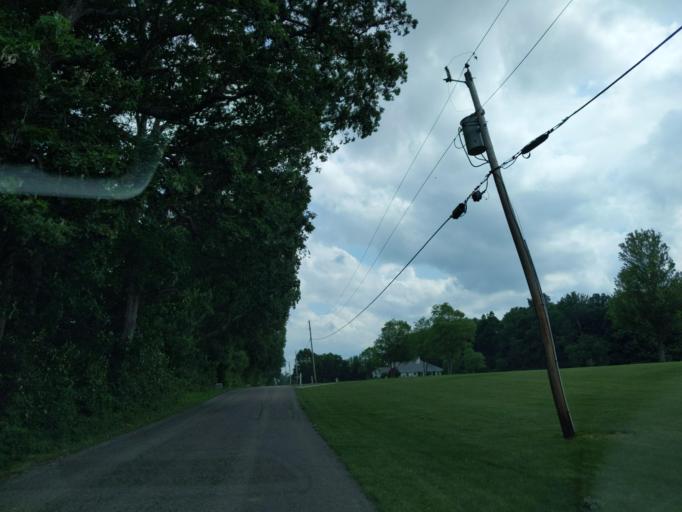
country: US
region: Indiana
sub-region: Ripley County
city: Batesville
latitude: 39.3265
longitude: -85.1899
